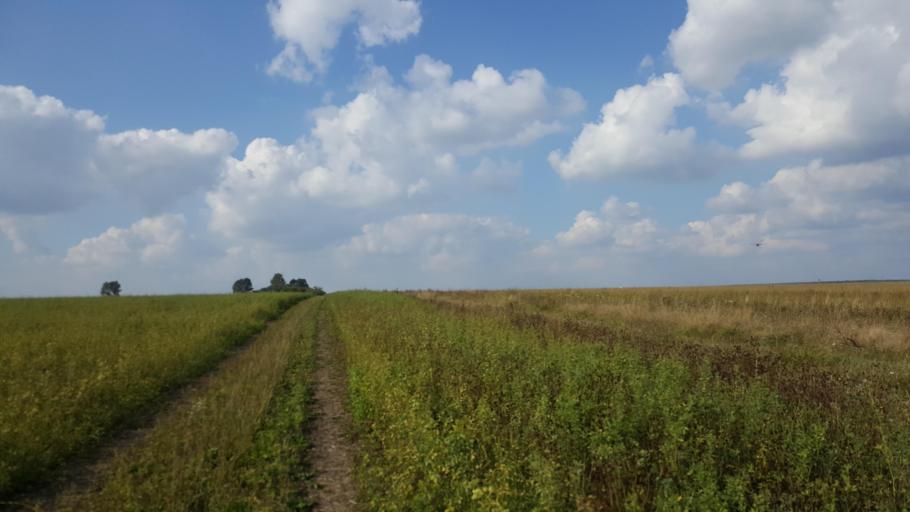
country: BY
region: Brest
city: Kamyanyets
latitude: 52.4196
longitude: 23.8143
